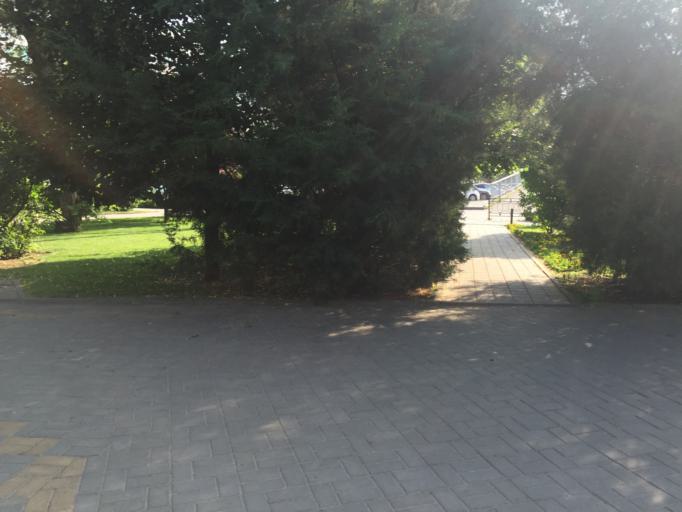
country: RU
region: Rostov
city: Rostov-na-Donu
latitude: 47.2127
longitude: 39.7077
